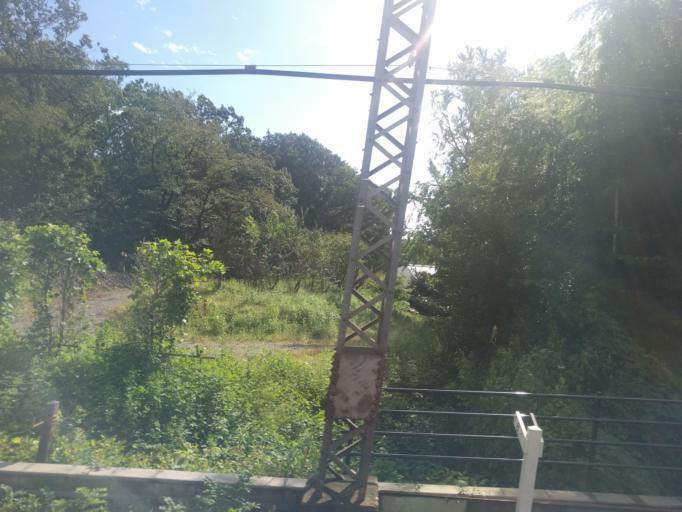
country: JP
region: Tokyo
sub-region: Machida-shi
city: Machida
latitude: 35.5392
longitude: 139.4427
